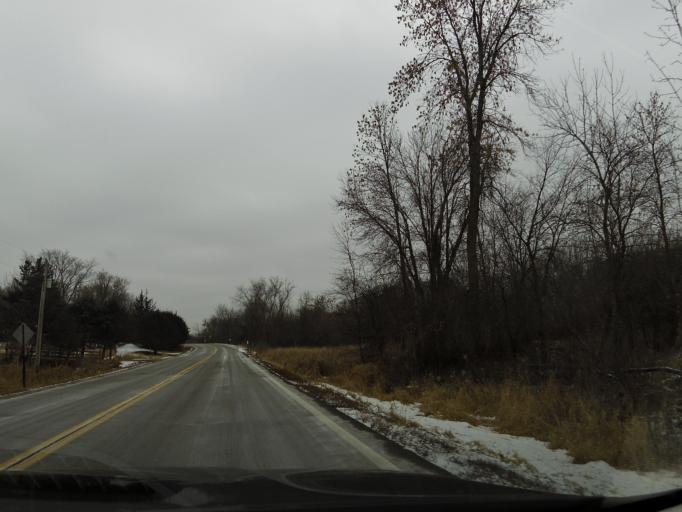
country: US
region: Minnesota
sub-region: Hennepin County
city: Medina
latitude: 45.0110
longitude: -93.6090
